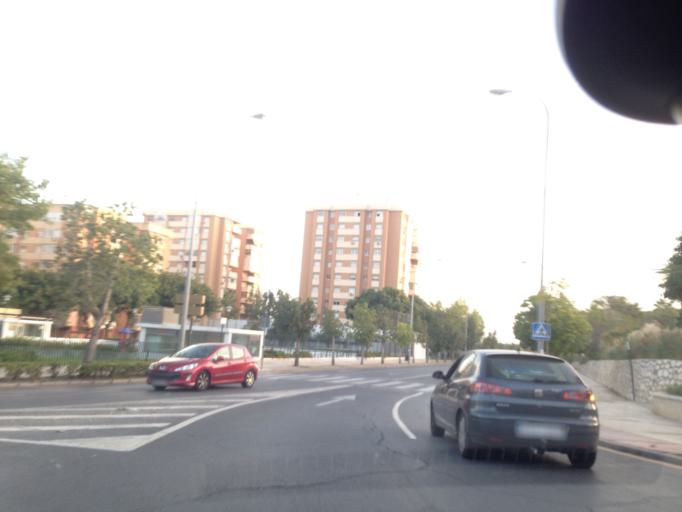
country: ES
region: Andalusia
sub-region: Provincia de Malaga
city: Malaga
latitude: 36.7335
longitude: -4.4337
